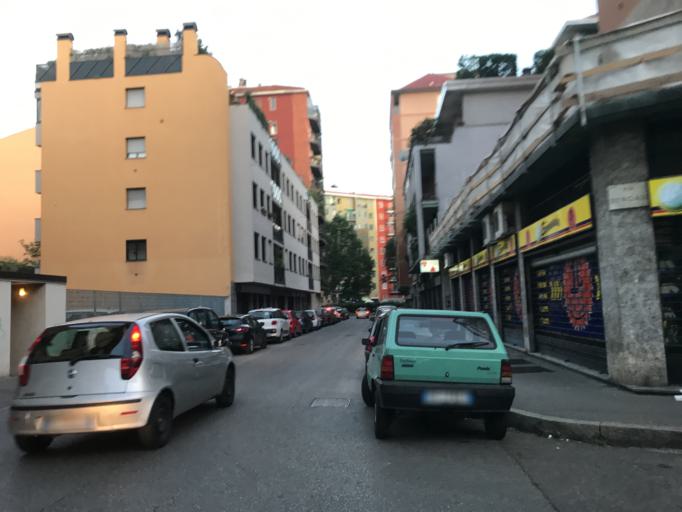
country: IT
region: Lombardy
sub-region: Citta metropolitana di Milano
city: Sesto San Giovanni
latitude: 45.4993
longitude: 9.2345
